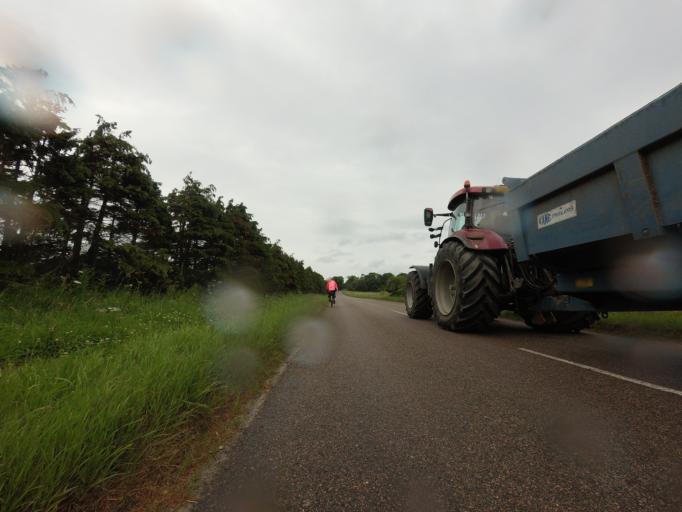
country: GB
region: Scotland
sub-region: Moray
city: Cullen
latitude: 57.6809
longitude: -2.8137
